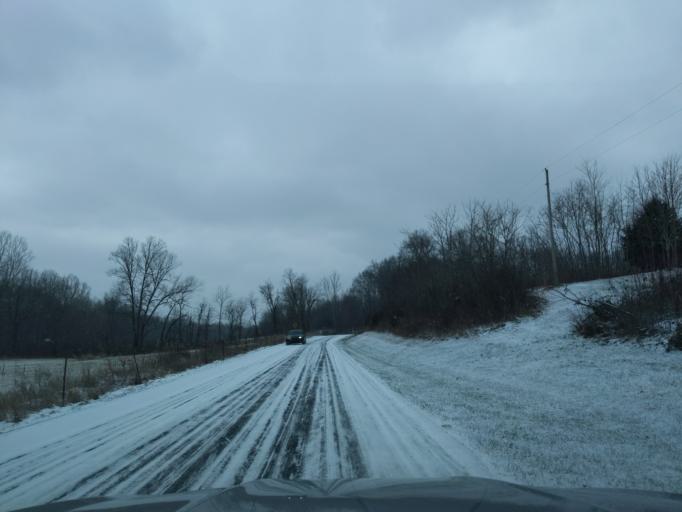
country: US
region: Indiana
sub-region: Decatur County
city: Westport
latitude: 39.2133
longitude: -85.5195
